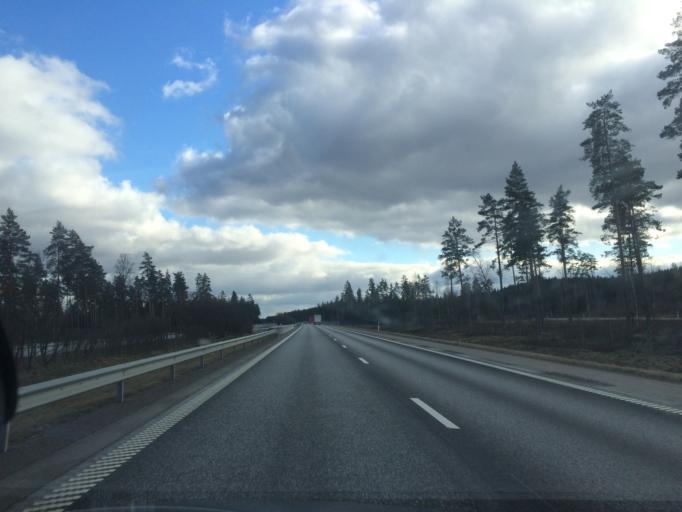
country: SE
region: Joenkoeping
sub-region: Vaggeryds Kommun
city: Skillingaryd
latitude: 57.3821
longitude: 14.1000
